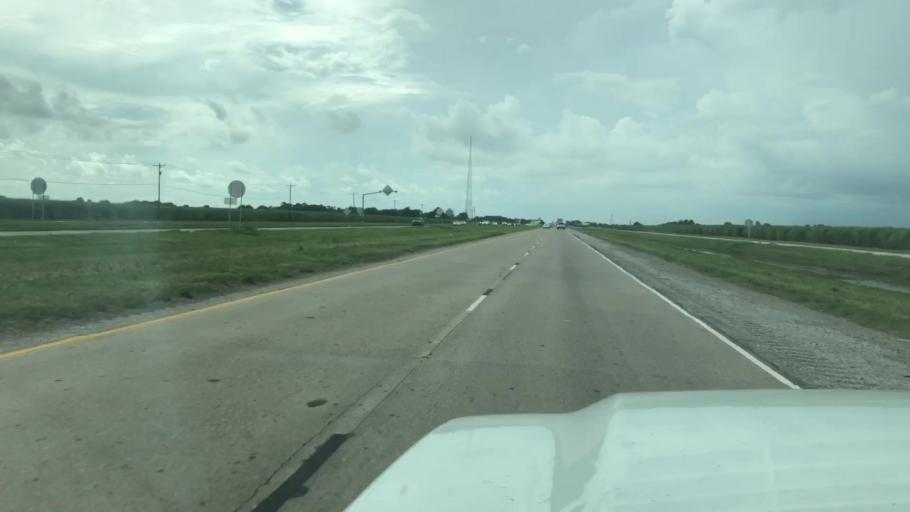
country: US
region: Louisiana
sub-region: Iberia Parish
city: Jeanerette
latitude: 29.9128
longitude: -91.7180
